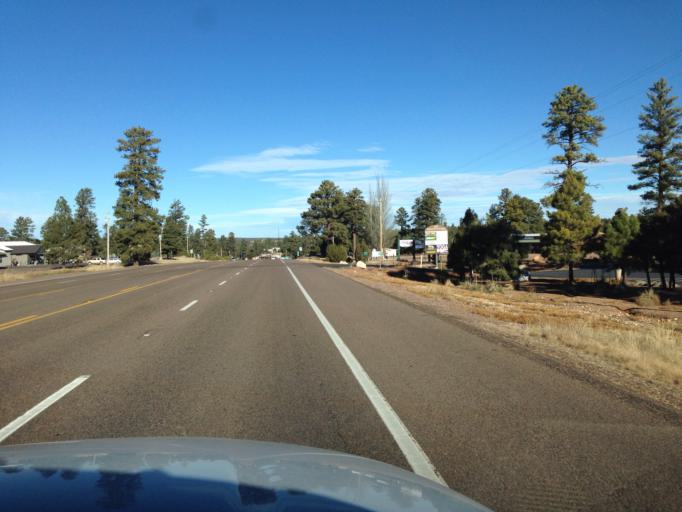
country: US
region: Arizona
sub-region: Navajo County
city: Heber-Overgaard
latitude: 34.4131
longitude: -110.5715
